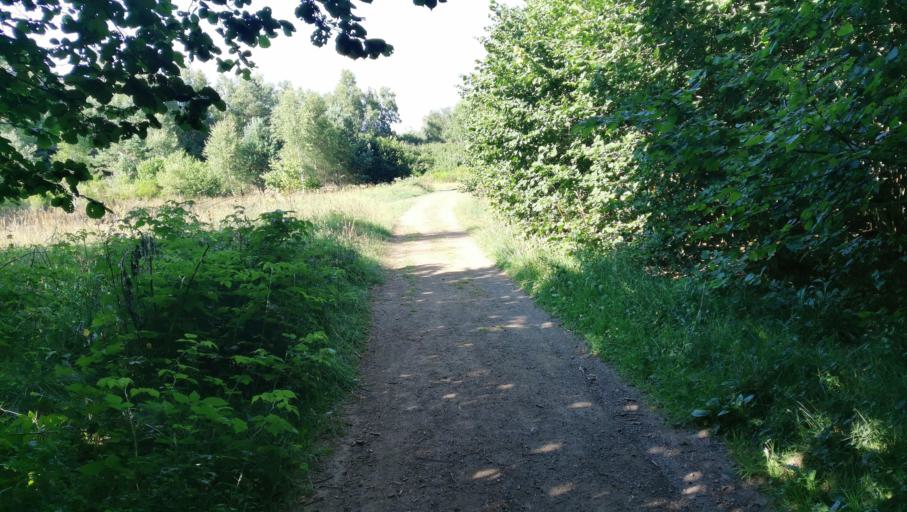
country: FR
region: Auvergne
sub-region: Departement du Puy-de-Dome
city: Orcines
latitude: 45.8016
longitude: 2.9663
